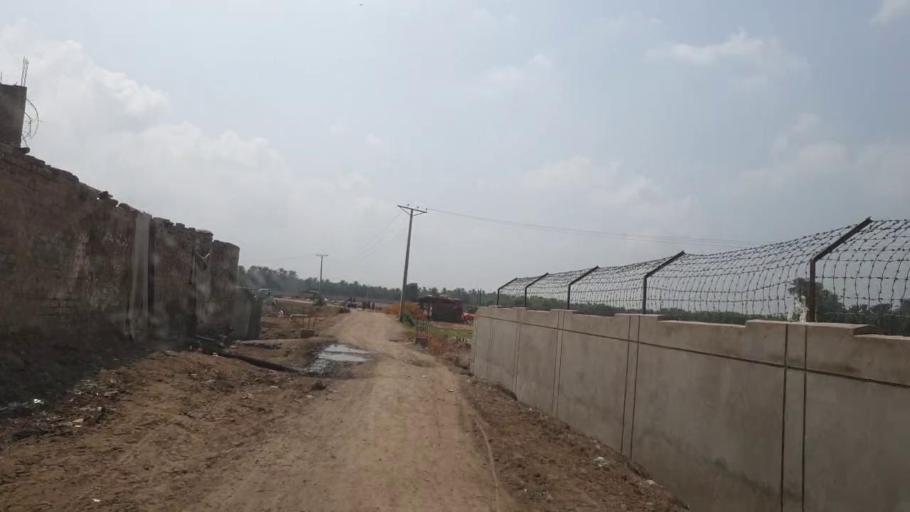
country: PK
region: Sindh
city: Khairpur
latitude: 27.5116
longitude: 68.7447
